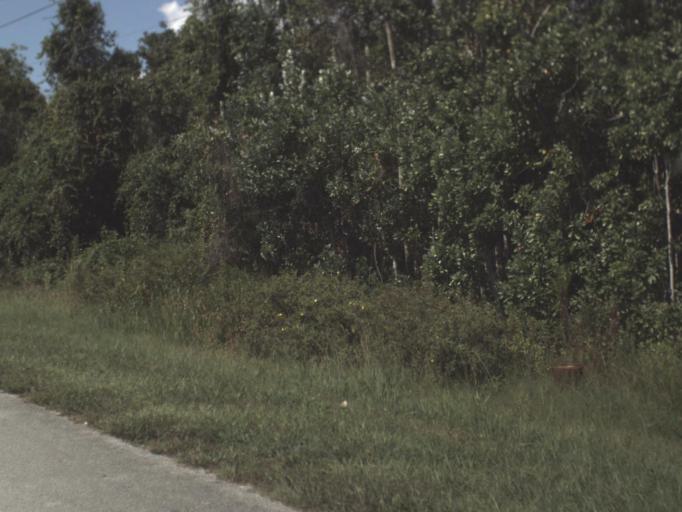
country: US
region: Florida
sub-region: Highlands County
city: Sebring
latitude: 27.4284
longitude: -81.3976
